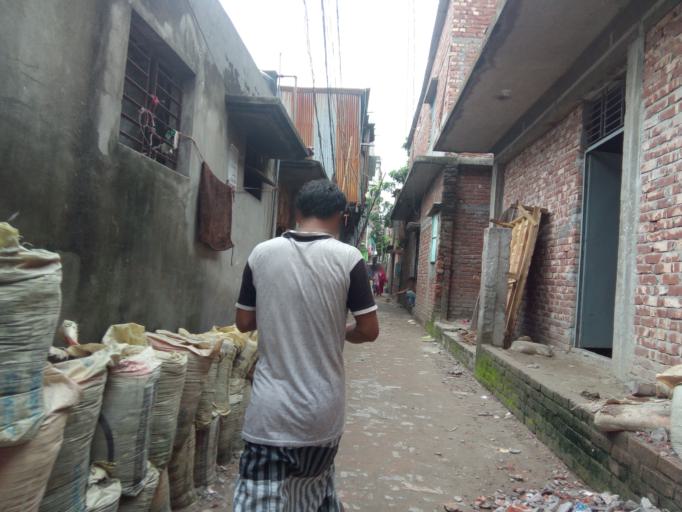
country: BD
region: Dhaka
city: Azimpur
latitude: 23.7169
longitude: 90.3762
